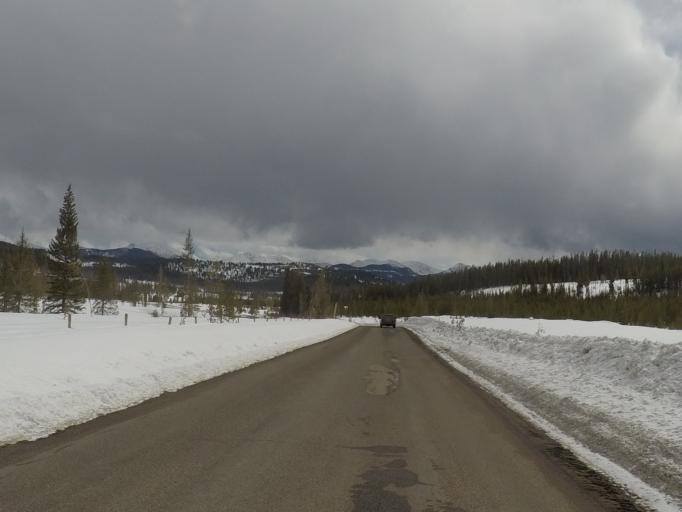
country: US
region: Montana
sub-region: Granite County
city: Philipsburg
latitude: 46.2141
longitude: -113.2576
